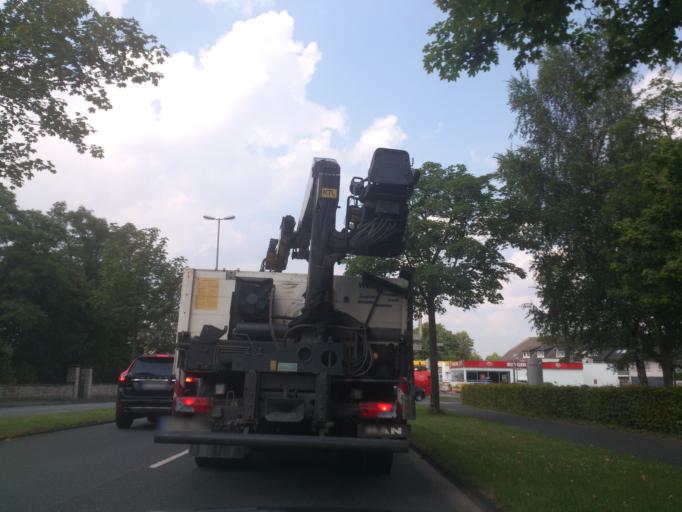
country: DE
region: North Rhine-Westphalia
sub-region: Regierungsbezirk Detmold
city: Paderborn
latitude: 51.7086
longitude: 8.7756
